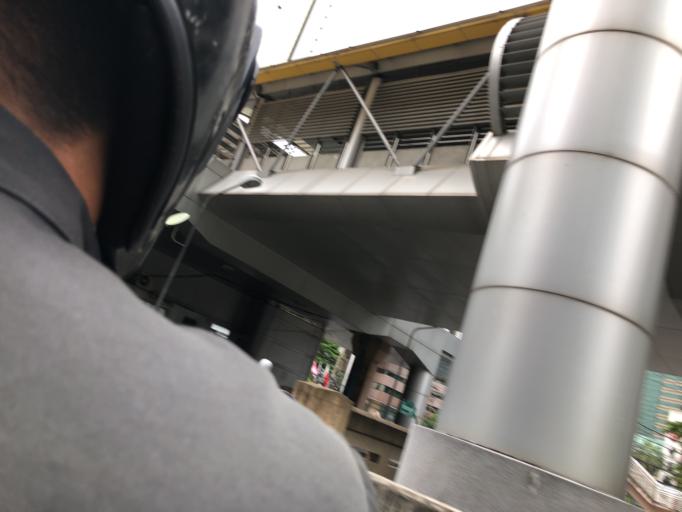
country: TH
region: Bangkok
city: Bang Rak
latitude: 13.7213
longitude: 100.5304
